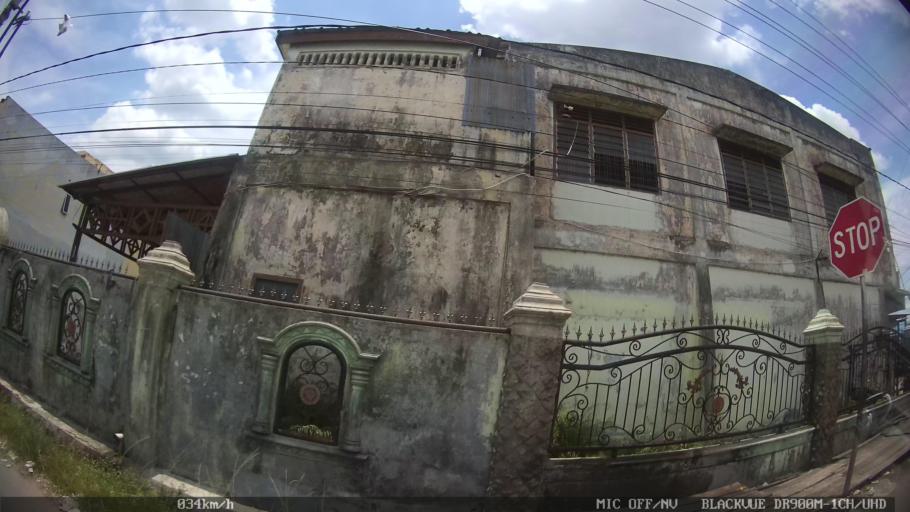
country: ID
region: North Sumatra
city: Binjai
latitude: 3.6279
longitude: 98.5092
